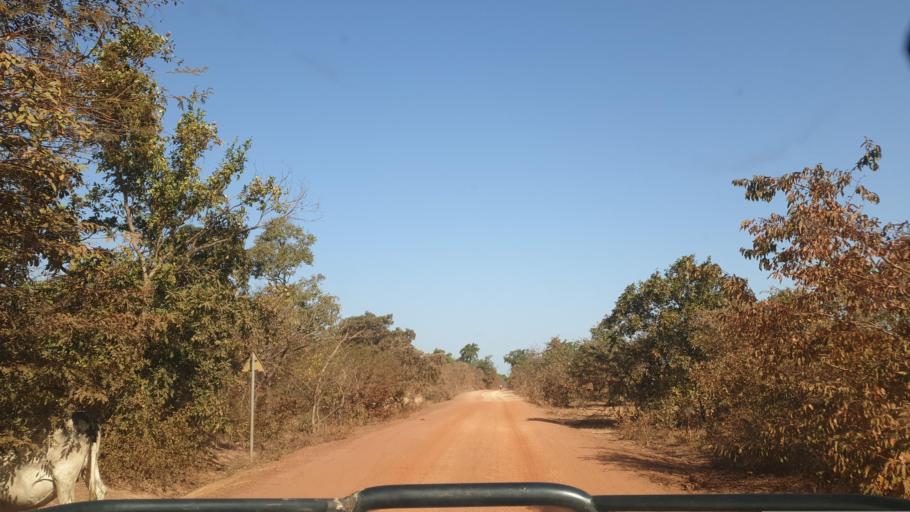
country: ML
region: Sikasso
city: Bougouni
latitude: 11.7791
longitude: -6.9078
